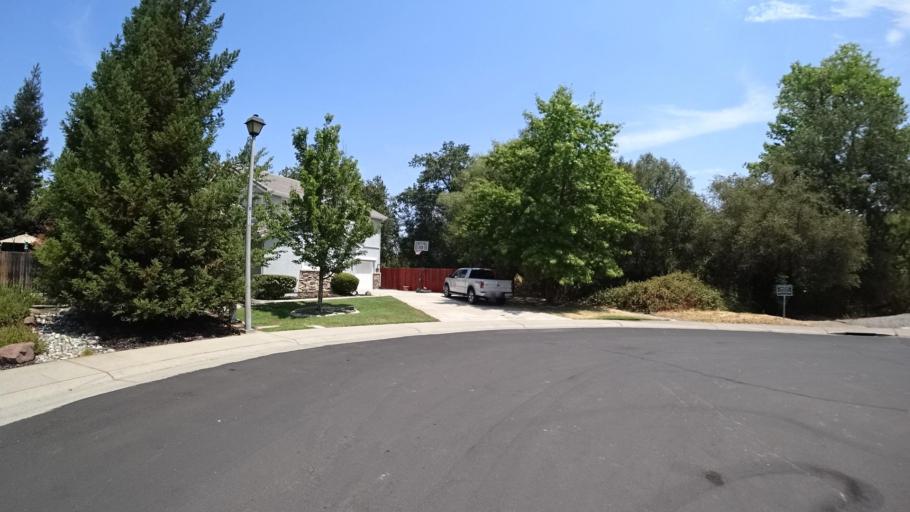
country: US
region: California
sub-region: Placer County
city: Rocklin
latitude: 38.8026
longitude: -121.2276
